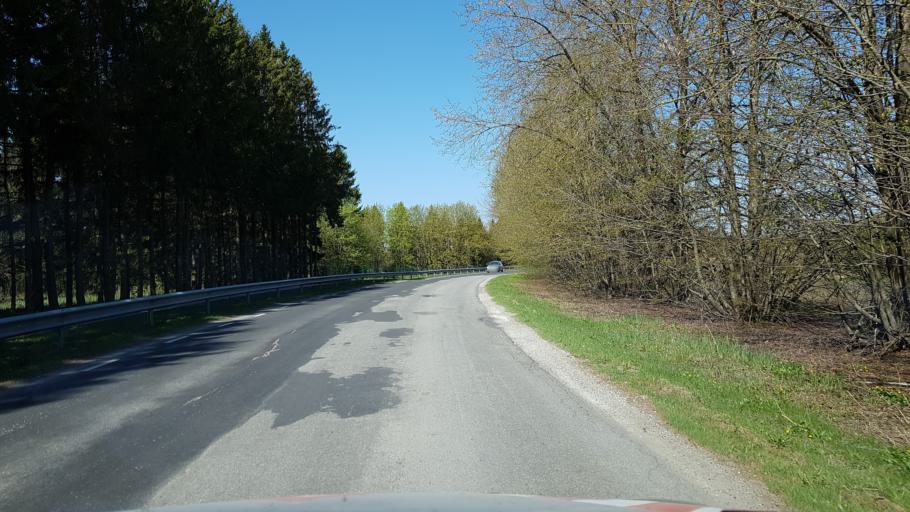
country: EE
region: Harju
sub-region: Joelaehtme vald
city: Loo
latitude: 59.4174
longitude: 24.9436
